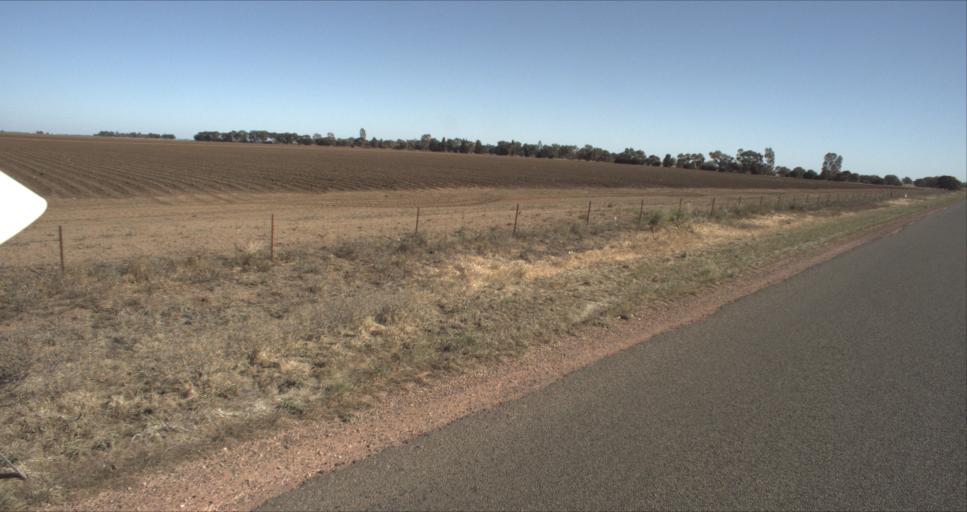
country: AU
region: New South Wales
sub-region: Leeton
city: Leeton
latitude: -34.5703
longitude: 146.2636
